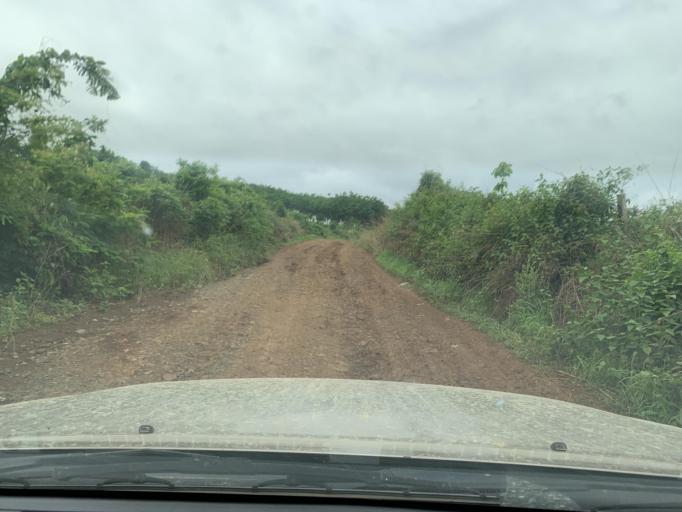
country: TH
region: Nan
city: Mae Charim
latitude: 18.4037
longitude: 101.4363
